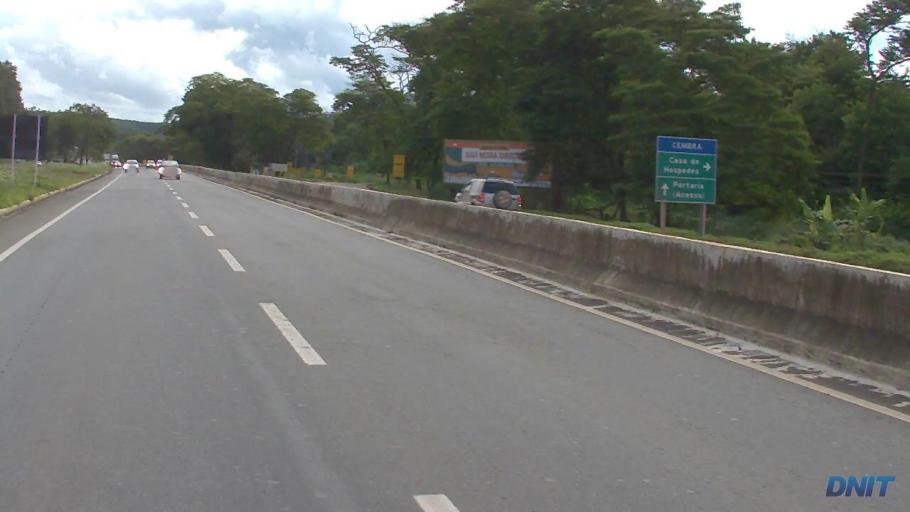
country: BR
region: Minas Gerais
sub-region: Ipaba
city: Ipaba
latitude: -19.3122
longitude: -42.3953
